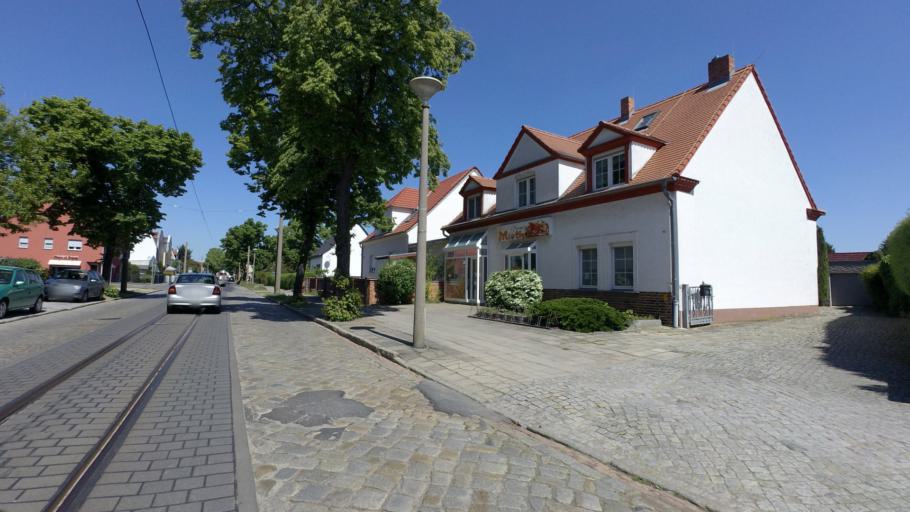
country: DE
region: Brandenburg
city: Cottbus
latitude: 51.7775
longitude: 14.3354
